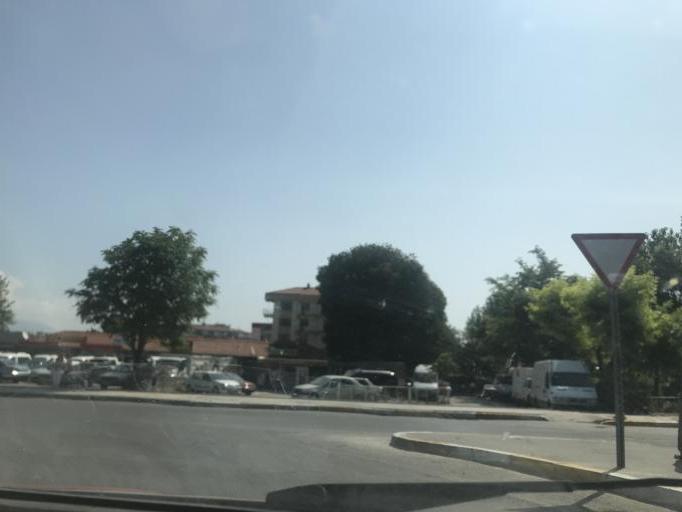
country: TR
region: Denizli
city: Denizli
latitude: 37.7788
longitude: 29.0979
